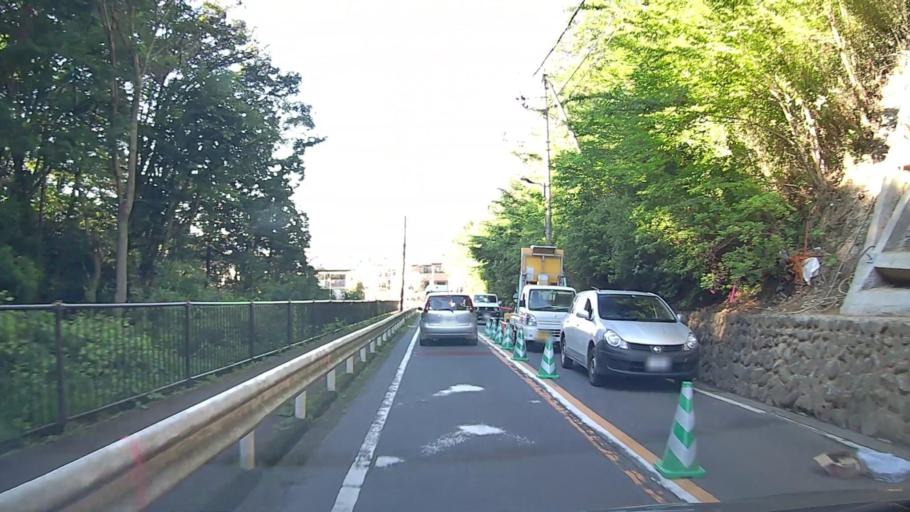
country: JP
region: Tokyo
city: Fussa
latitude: 35.7815
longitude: 139.3636
